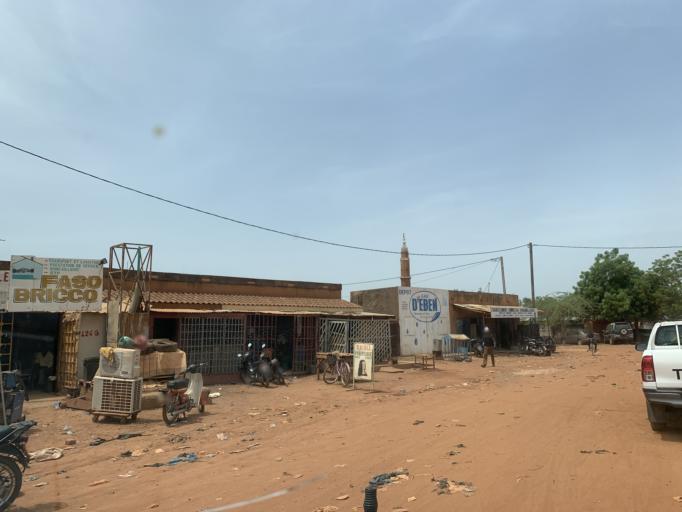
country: BF
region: Centre
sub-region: Kadiogo Province
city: Ouagadougou
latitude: 12.3282
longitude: -1.4869
